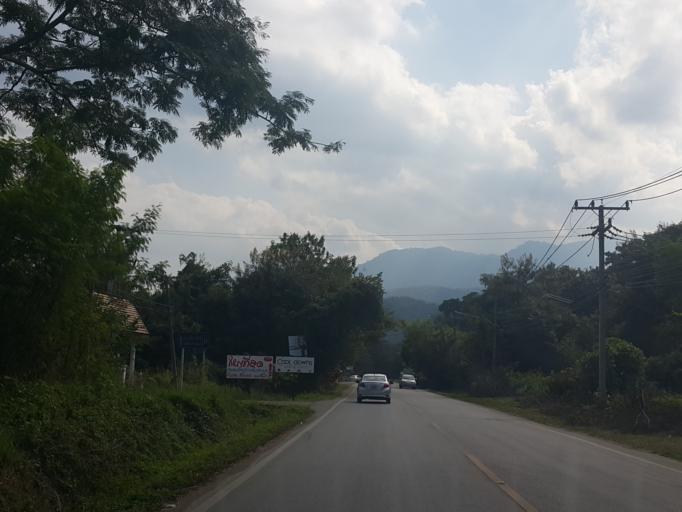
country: TH
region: Chiang Mai
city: Chiang Mai
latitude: 18.9135
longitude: 98.9057
